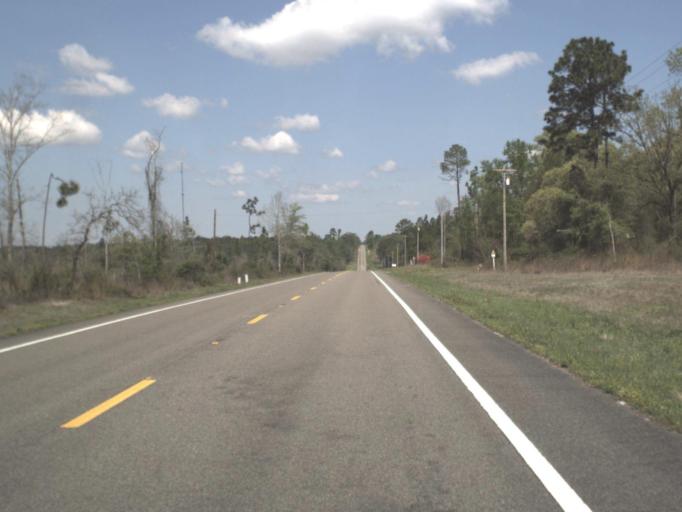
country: US
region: Alabama
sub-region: Escambia County
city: East Brewton
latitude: 30.9150
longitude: -87.0427
